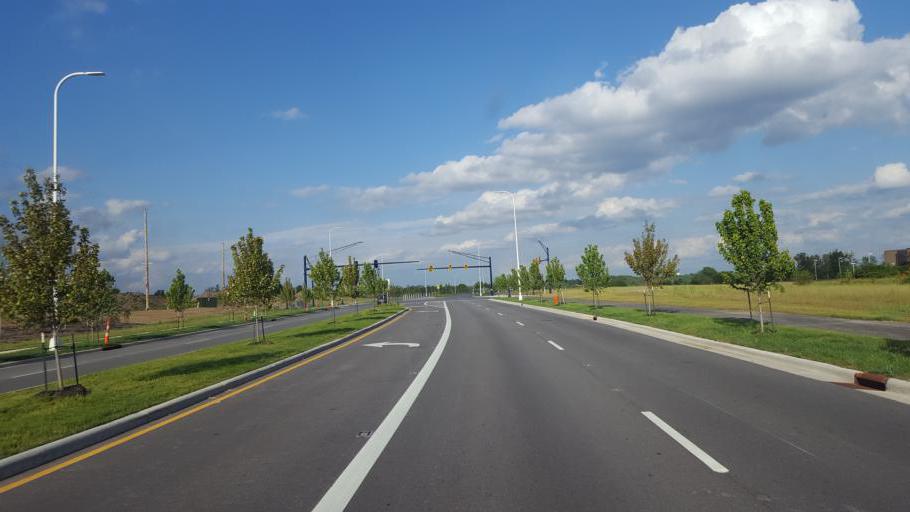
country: US
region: Ohio
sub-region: Franklin County
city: Westerville
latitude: 40.1480
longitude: -82.9655
